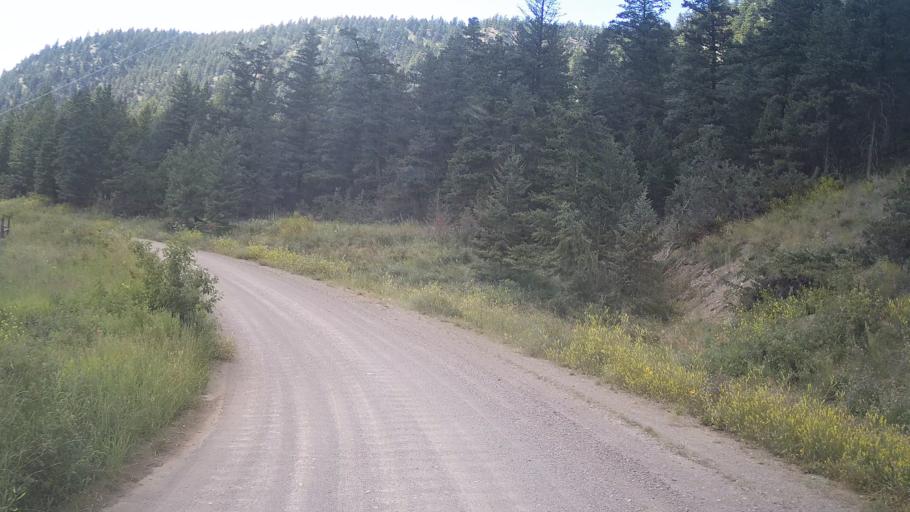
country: CA
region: British Columbia
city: Lillooet
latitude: 51.2520
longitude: -122.0202
